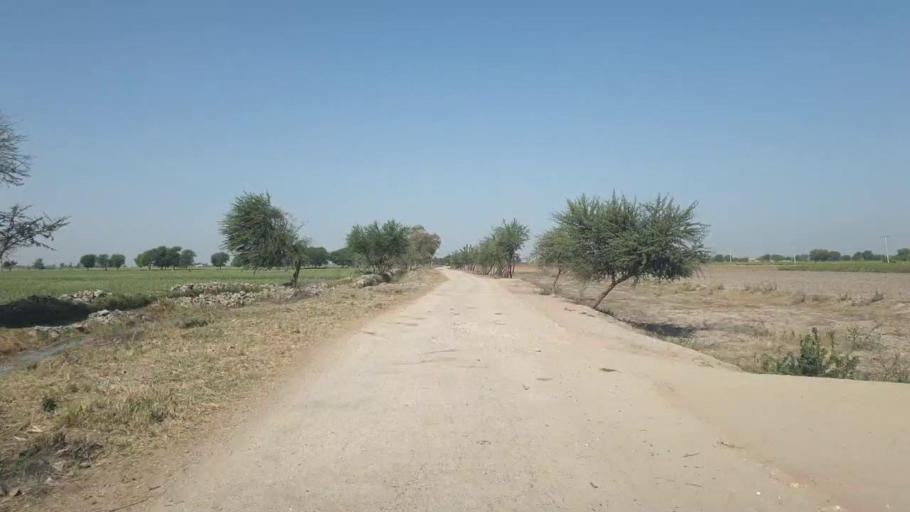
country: PK
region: Sindh
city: Umarkot
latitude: 25.2990
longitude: 69.6229
